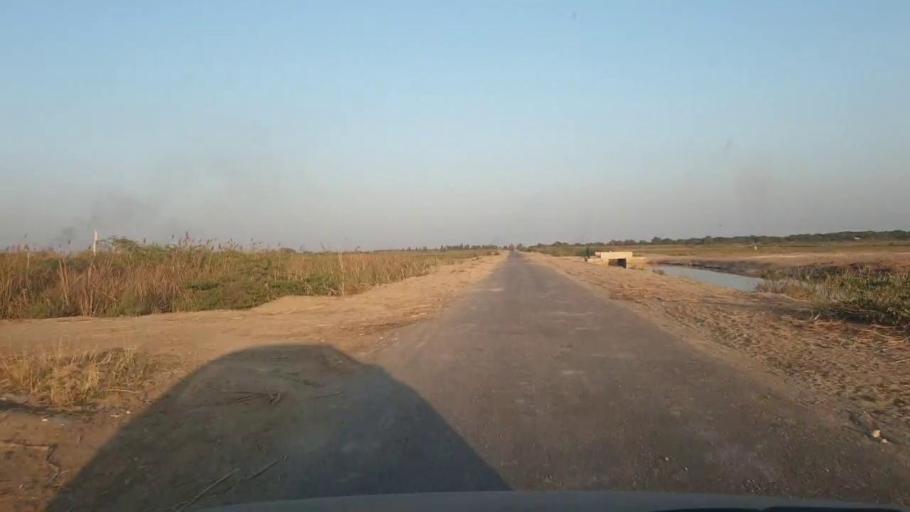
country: PK
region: Sindh
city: Chambar
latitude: 25.2775
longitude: 68.9182
